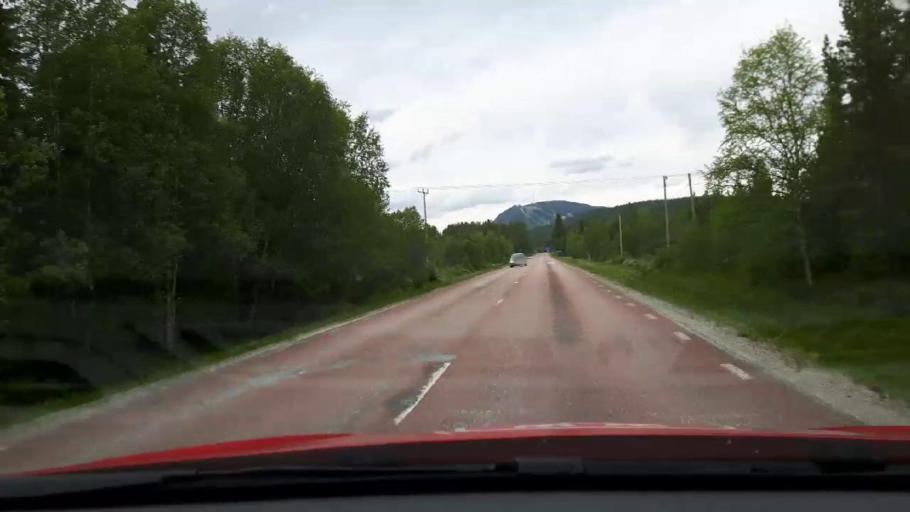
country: NO
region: Hedmark
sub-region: Engerdal
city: Engerdal
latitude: 62.5166
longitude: 12.6003
